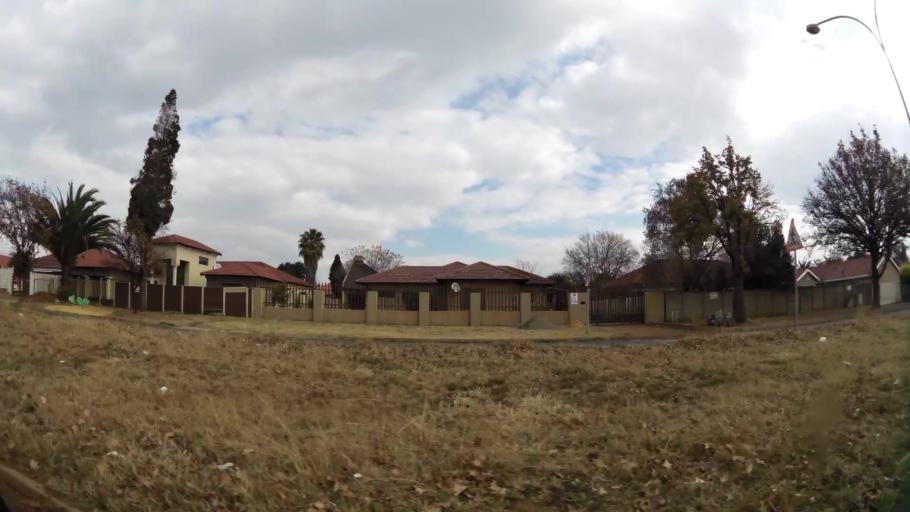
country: ZA
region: Gauteng
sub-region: Sedibeng District Municipality
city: Vanderbijlpark
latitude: -26.7227
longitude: 27.8629
